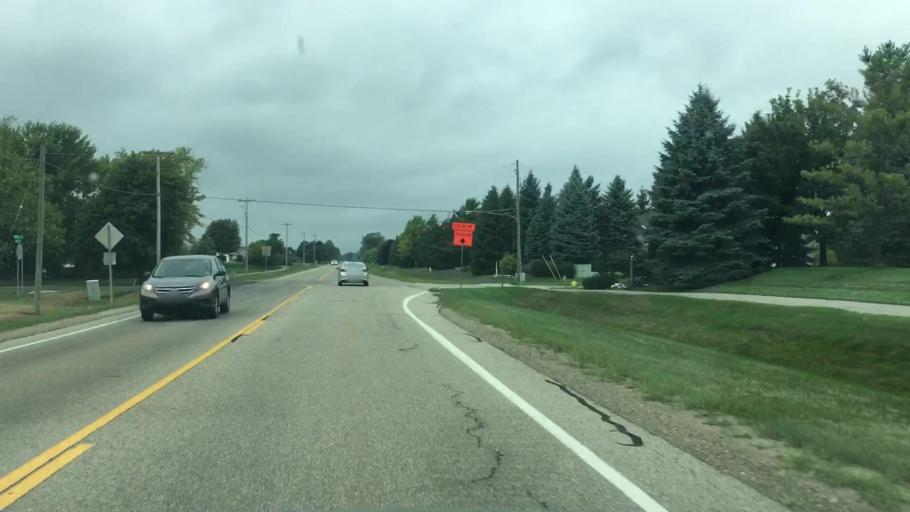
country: US
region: Michigan
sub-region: Ottawa County
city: Hudsonville
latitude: 42.8708
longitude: -85.8210
